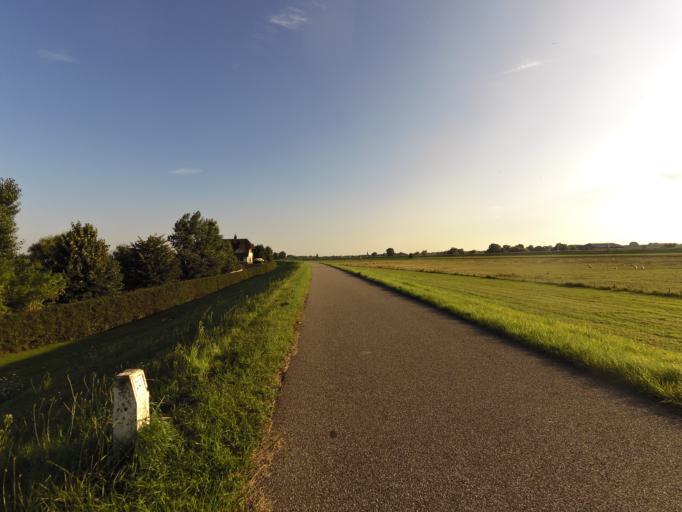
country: NL
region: Gelderland
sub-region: Gemeente Westervoort
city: Westervoort
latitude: 51.9596
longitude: 5.9552
